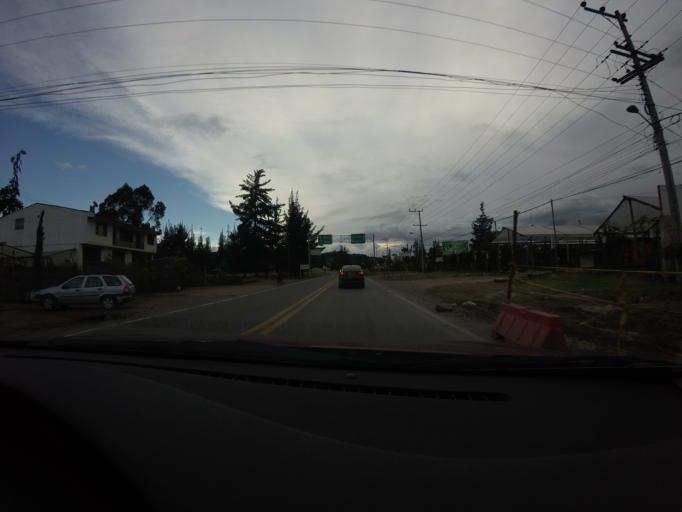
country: CO
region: Cundinamarca
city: Sopo
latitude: 4.9411
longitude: -73.9632
